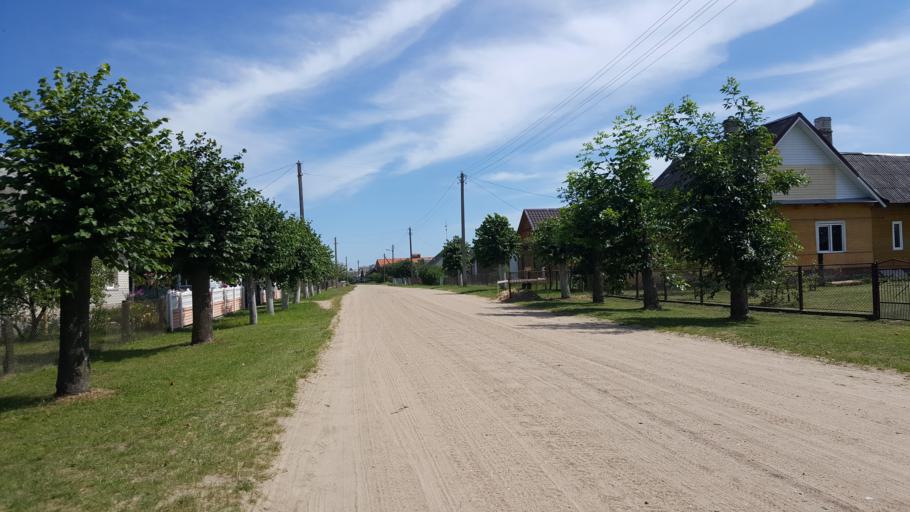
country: BY
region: Brest
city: Pruzhany
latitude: 52.5625
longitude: 24.2070
